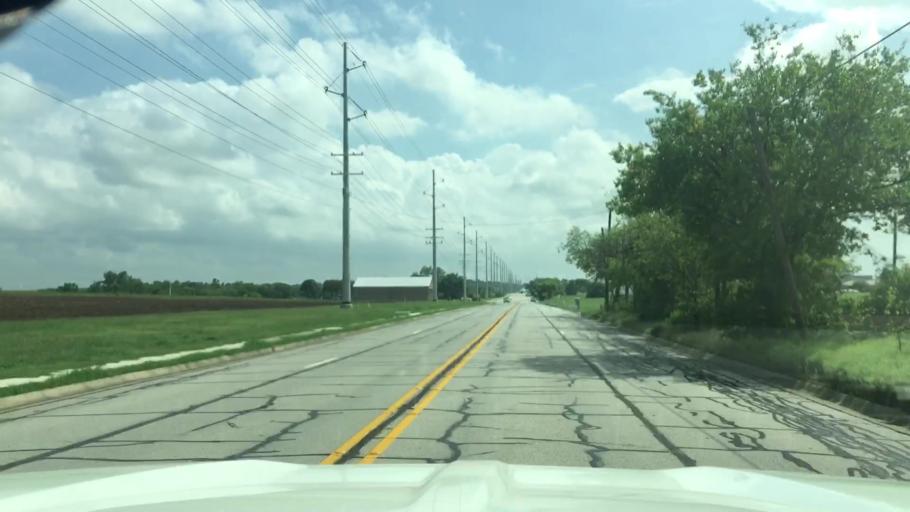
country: US
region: Texas
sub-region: Denton County
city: Denton
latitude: 33.2429
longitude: -97.1607
